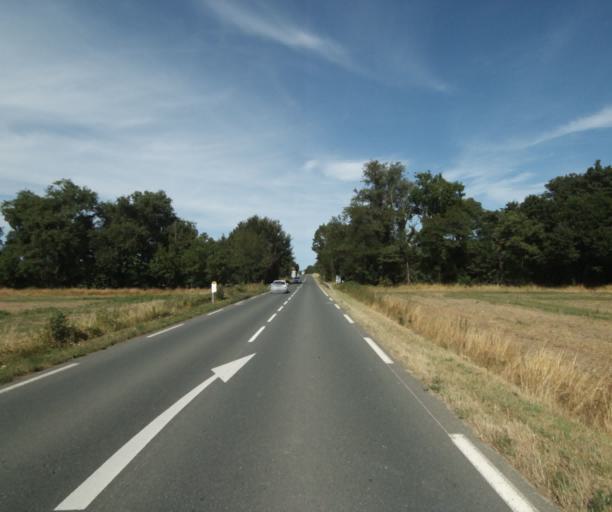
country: FR
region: Midi-Pyrenees
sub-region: Departement du Tarn
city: Soual
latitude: 43.5259
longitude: 2.0934
